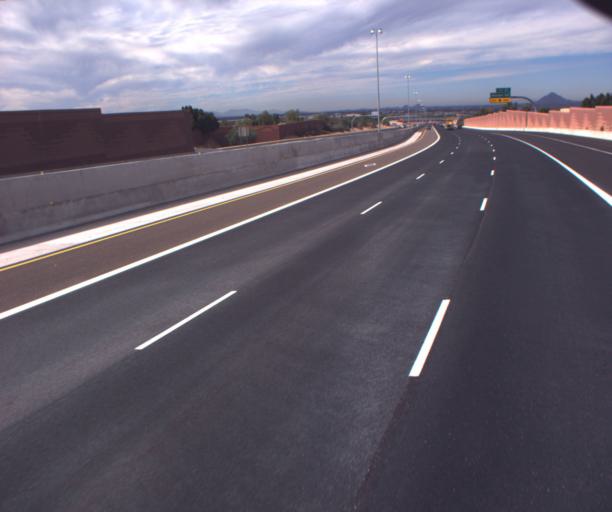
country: US
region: Arizona
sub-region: Maricopa County
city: Fountain Hills
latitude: 33.4755
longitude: -111.6898
